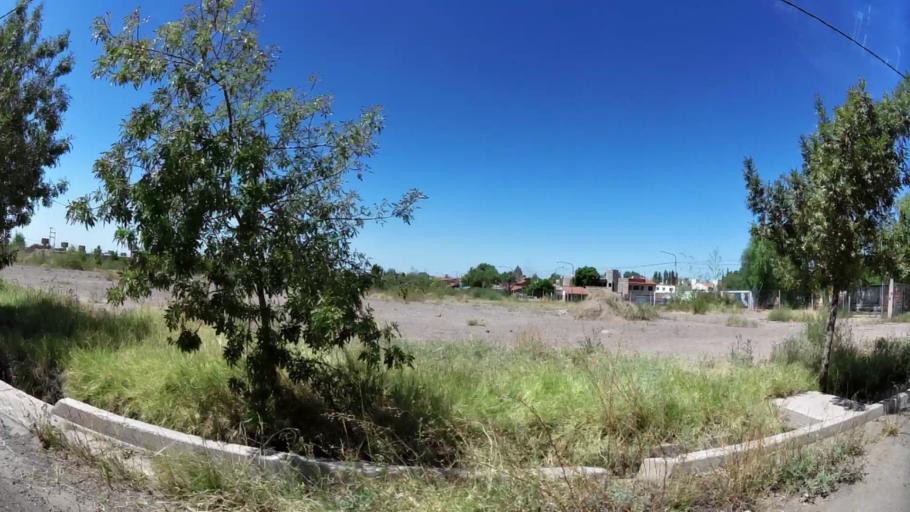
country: AR
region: Mendoza
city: Las Heras
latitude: -32.8516
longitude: -68.8575
